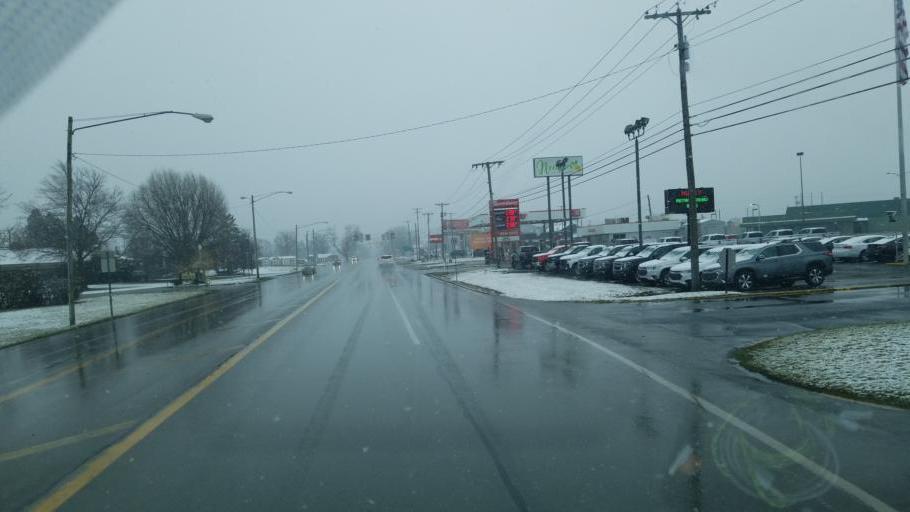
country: US
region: Indiana
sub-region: Grant County
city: Marion
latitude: 40.5769
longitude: -85.6757
